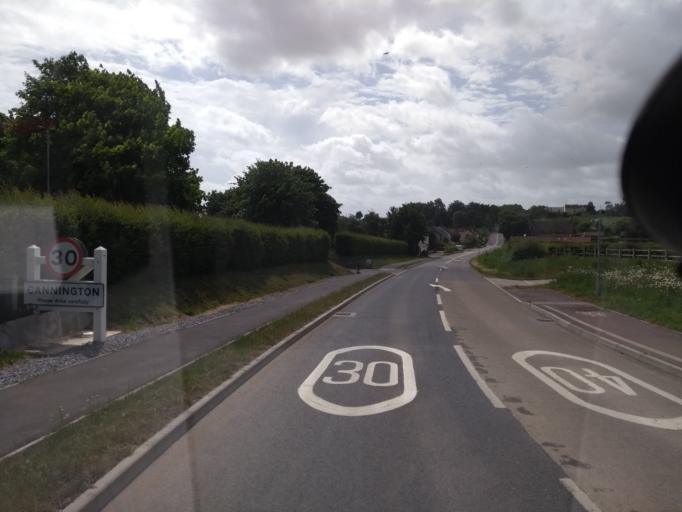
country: GB
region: England
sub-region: Somerset
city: Bridgwater
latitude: 51.1587
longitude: -3.0655
